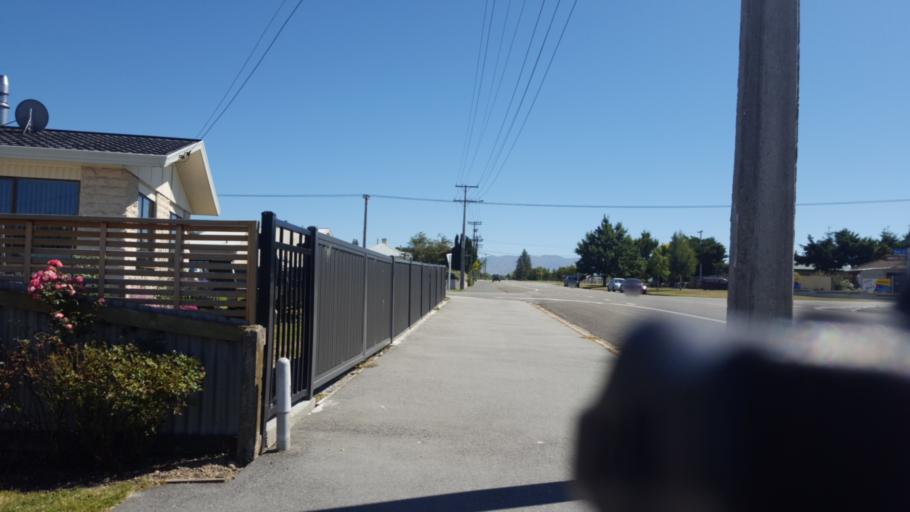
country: NZ
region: Otago
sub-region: Dunedin City
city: Dunedin
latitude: -45.1272
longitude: 170.1005
